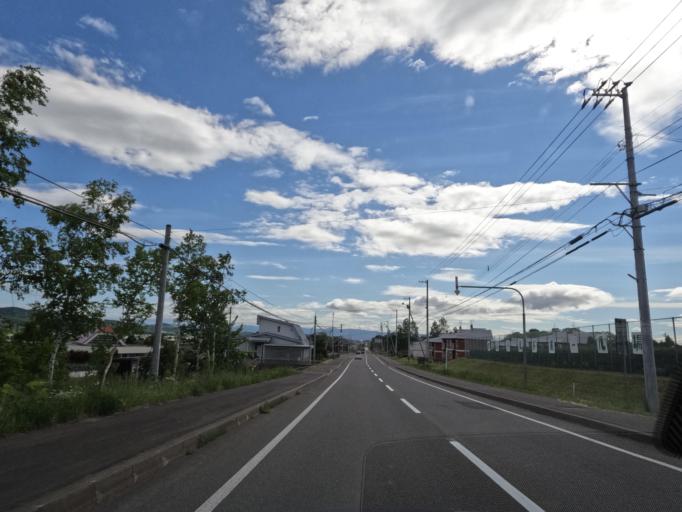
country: JP
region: Hokkaido
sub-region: Asahikawa-shi
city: Asahikawa
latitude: 43.8321
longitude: 142.5318
